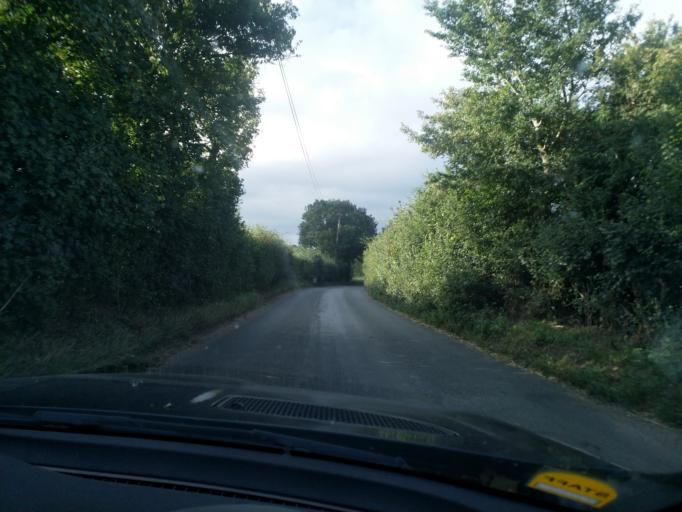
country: GB
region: England
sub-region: Suffolk
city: Elmswell
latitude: 52.2309
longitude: 0.9458
